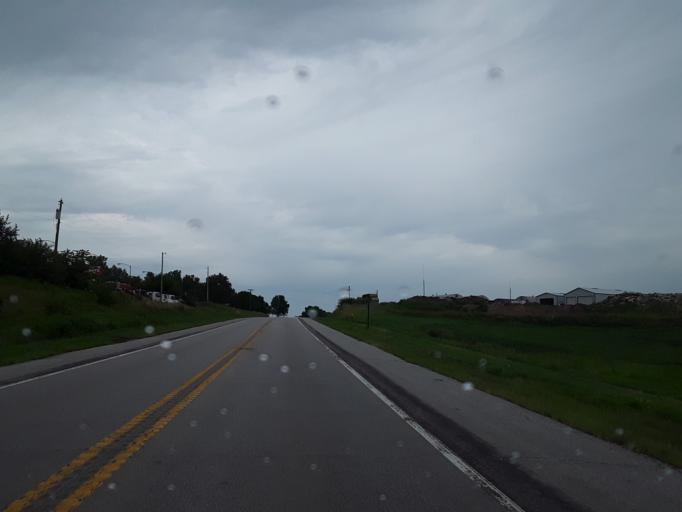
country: US
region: Nebraska
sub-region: Washington County
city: Blair
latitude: 41.5046
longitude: -96.1589
